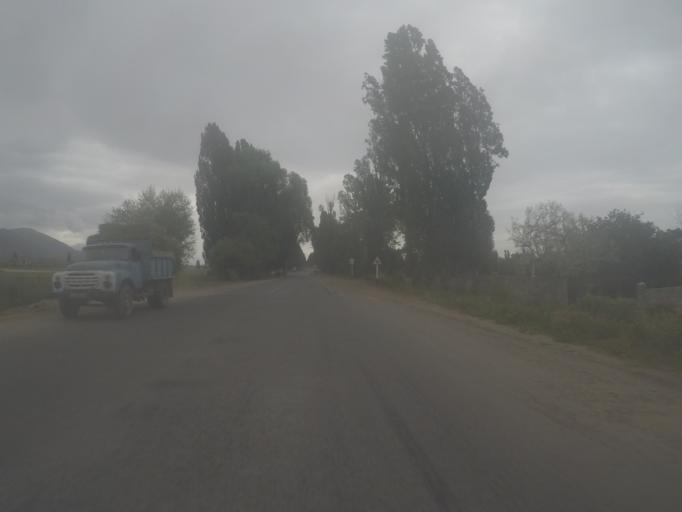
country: KG
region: Ysyk-Koel
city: Cholpon-Ata
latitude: 42.6915
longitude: 77.3713
